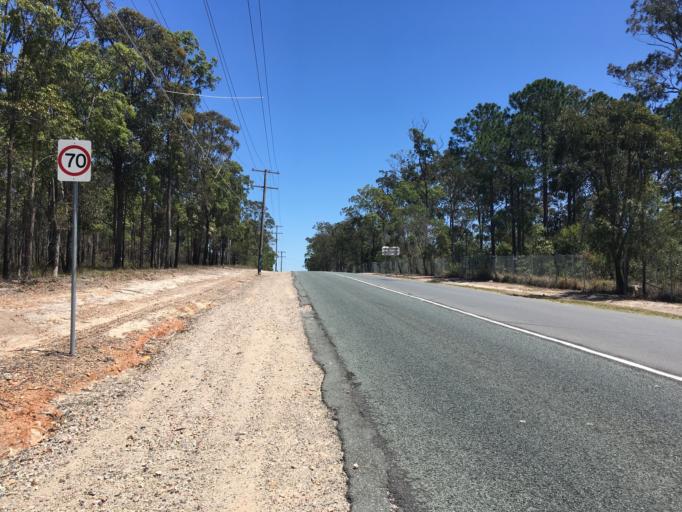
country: AU
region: Queensland
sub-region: Logan
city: Logan Reserve
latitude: -27.6939
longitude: 153.0766
